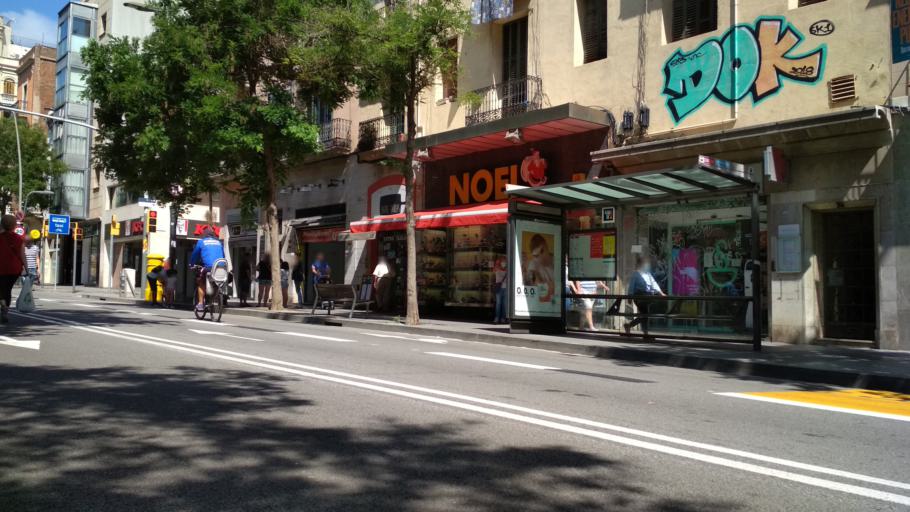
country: ES
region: Catalonia
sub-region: Provincia de Barcelona
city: les Corts
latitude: 41.3754
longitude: 2.1395
